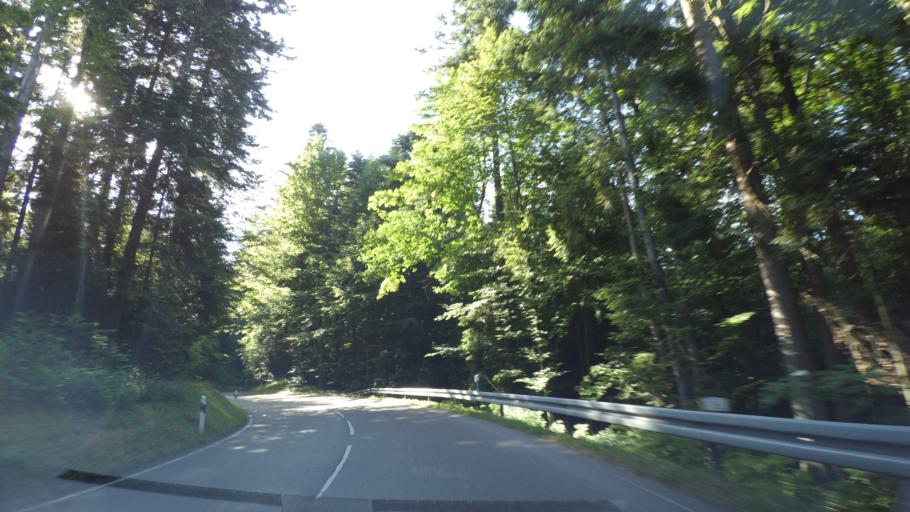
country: DE
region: Baden-Wuerttemberg
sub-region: Regierungsbezirk Stuttgart
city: Welzheim
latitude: 48.8994
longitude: 9.6623
